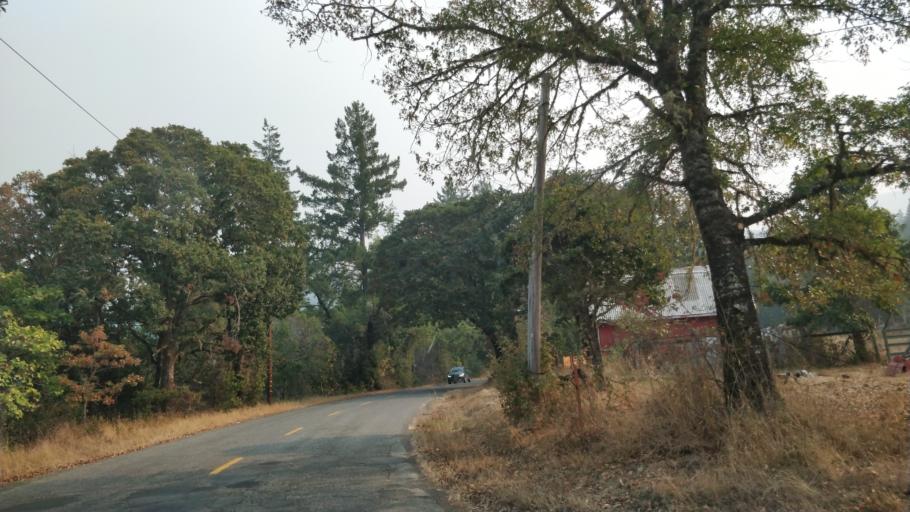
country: US
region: California
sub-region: Humboldt County
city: Rio Dell
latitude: 40.2344
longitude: -124.1554
